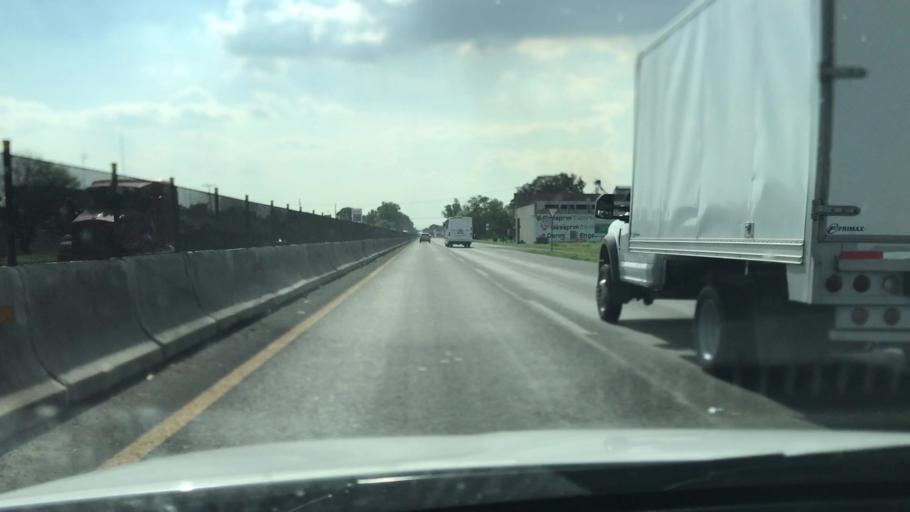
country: MX
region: Guanajuato
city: Valtierrilla
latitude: 20.5494
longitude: -101.1406
